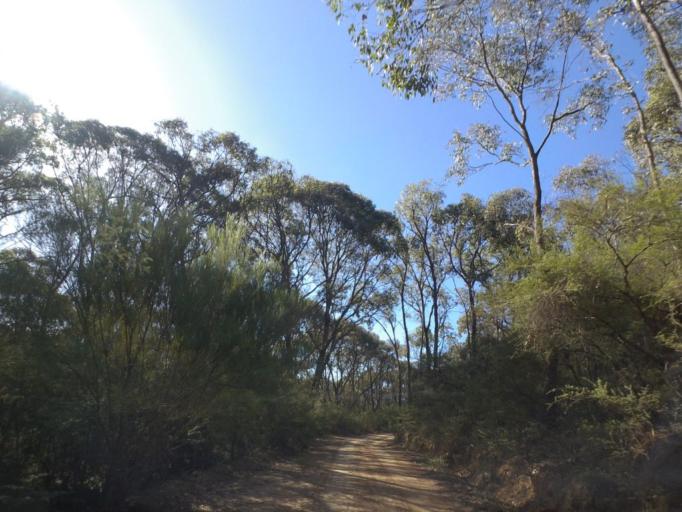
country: AU
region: Victoria
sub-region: Murrindindi
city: Kinglake West
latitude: -37.4700
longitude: 145.3644
